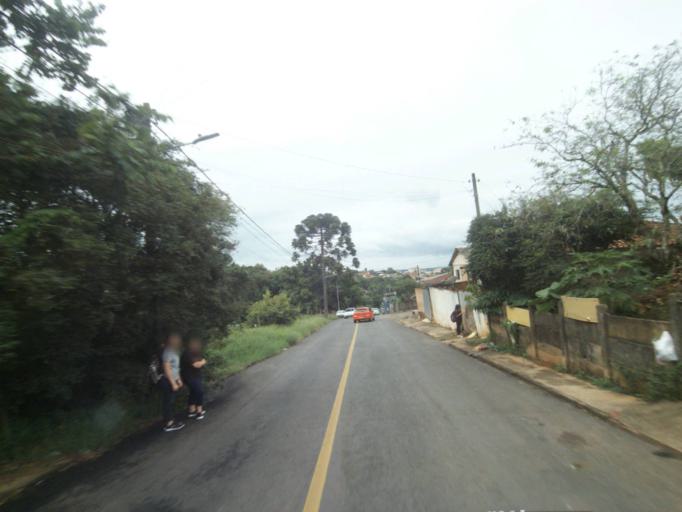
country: BR
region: Parana
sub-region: Telemaco Borba
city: Telemaco Borba
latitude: -24.3284
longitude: -50.6457
